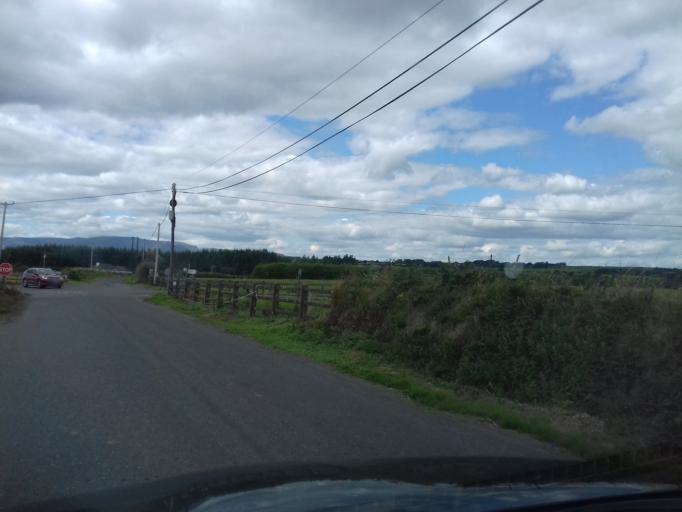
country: IE
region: Munster
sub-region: Waterford
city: Portlaw
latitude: 52.1821
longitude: -7.2993
